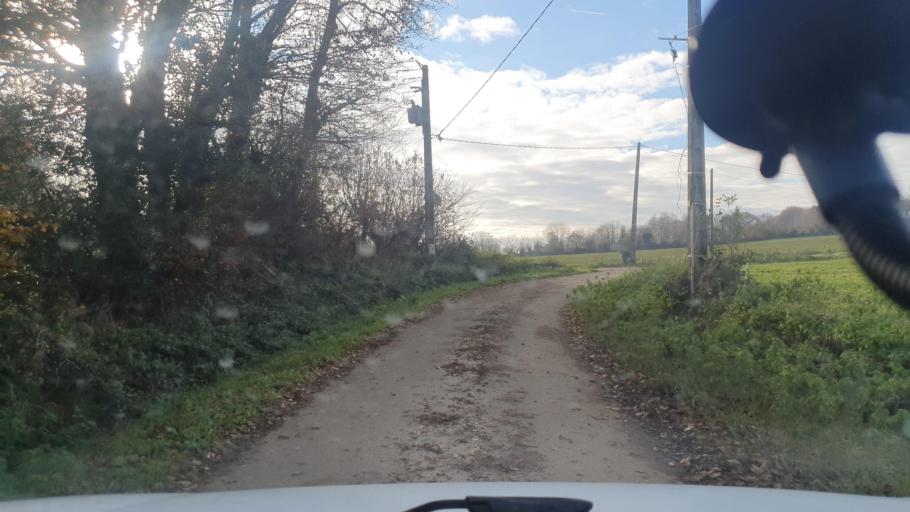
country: FR
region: Brittany
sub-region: Departement du Finistere
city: Briec
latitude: 48.0947
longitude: -4.0115
